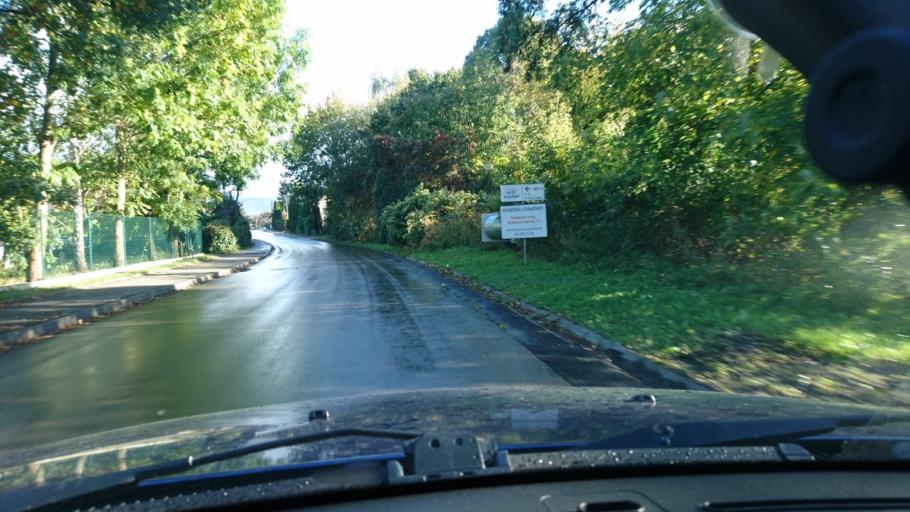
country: PL
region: Silesian Voivodeship
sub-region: Bielsko-Biala
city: Bielsko-Biala
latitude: 49.8465
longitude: 19.0477
